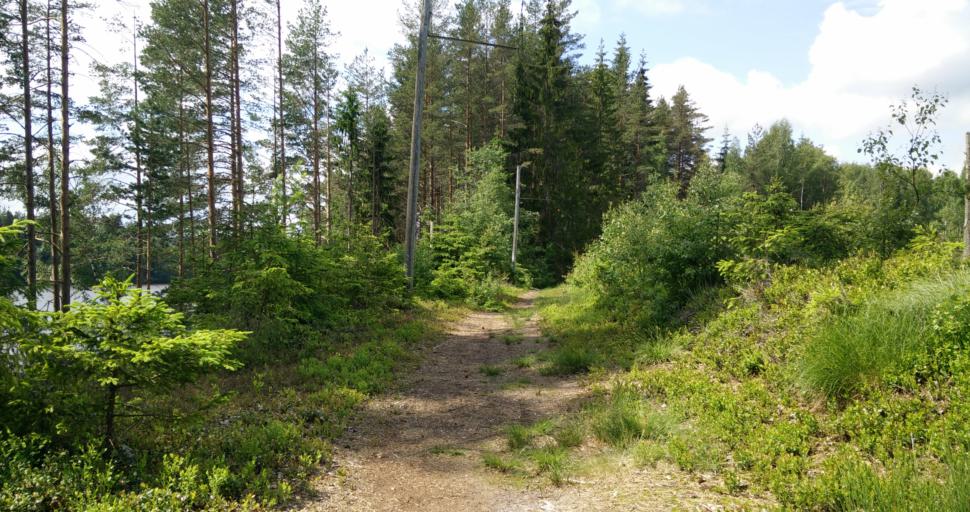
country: SE
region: Vaermland
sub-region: Hagfors Kommun
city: Hagfors
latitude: 60.0109
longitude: 13.5776
